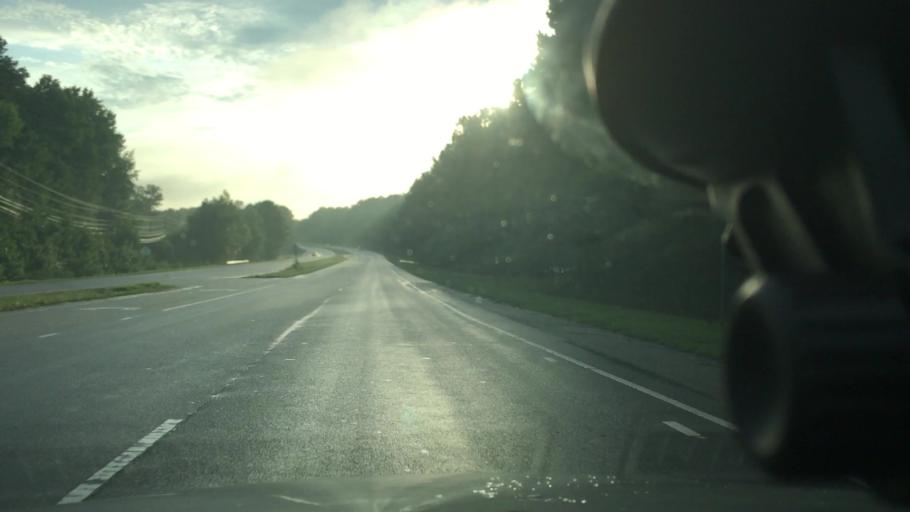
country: US
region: North Carolina
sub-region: Wilson County
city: Wilson
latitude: 35.7642
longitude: -78.0119
